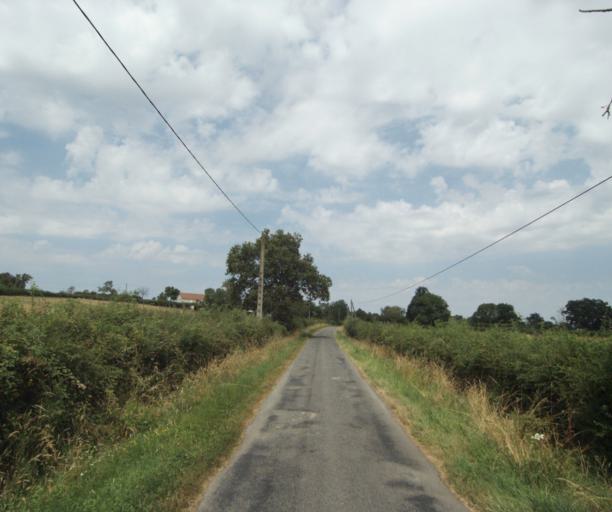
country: FR
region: Bourgogne
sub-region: Departement de Saone-et-Loire
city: Gueugnon
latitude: 46.5877
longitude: 4.0407
